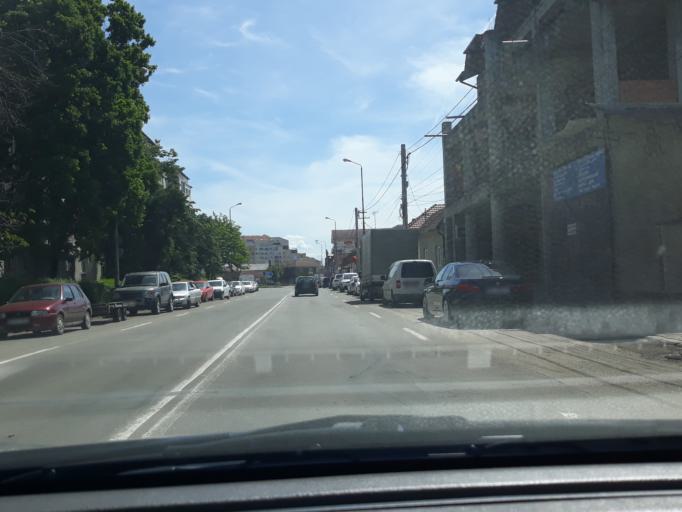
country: RO
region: Bihor
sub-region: Comuna Biharea
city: Oradea
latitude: 47.0653
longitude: 21.9025
